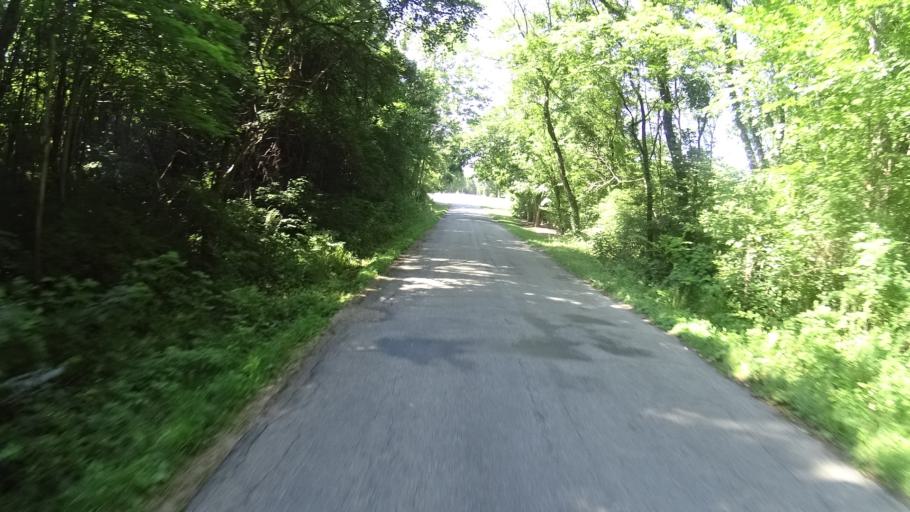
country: US
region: Indiana
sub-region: Madison County
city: Ingalls
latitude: 39.9607
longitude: -85.8150
